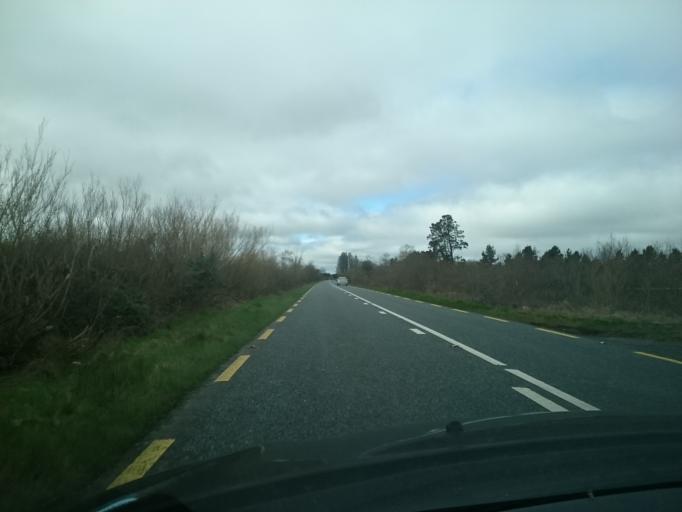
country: IE
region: Connaught
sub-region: Maigh Eo
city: Claremorris
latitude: 53.7168
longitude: -8.8940
